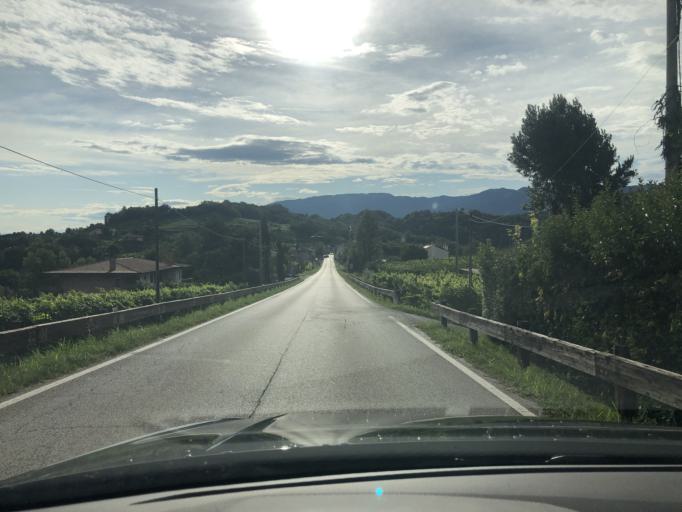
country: IT
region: Veneto
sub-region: Provincia di Treviso
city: Corbanese
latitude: 45.9332
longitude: 12.2341
